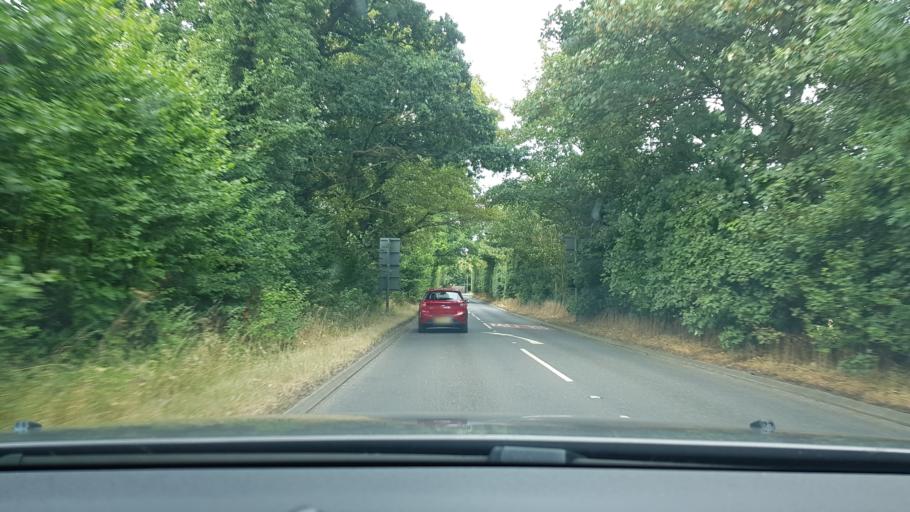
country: GB
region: England
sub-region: West Berkshire
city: Hungerford
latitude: 51.4269
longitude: -1.5013
